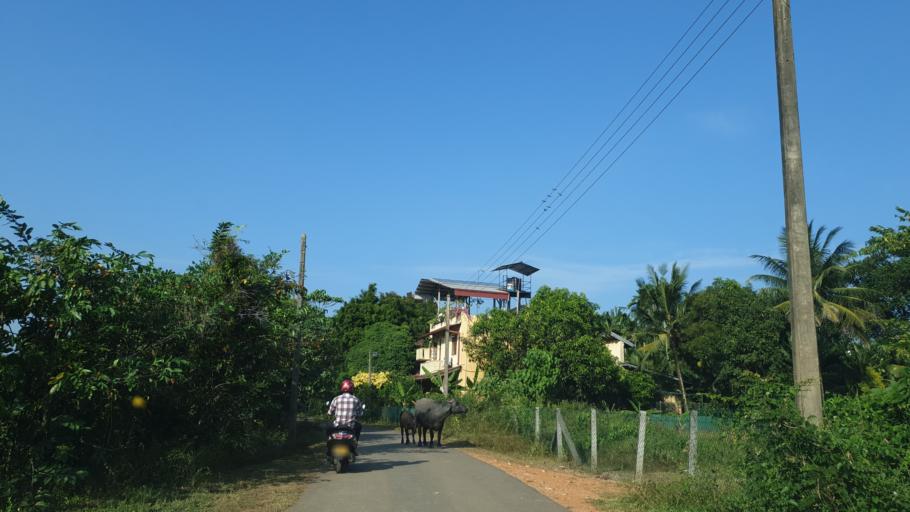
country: LK
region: Western
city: Battaramulla South
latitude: 6.8840
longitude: 79.9483
